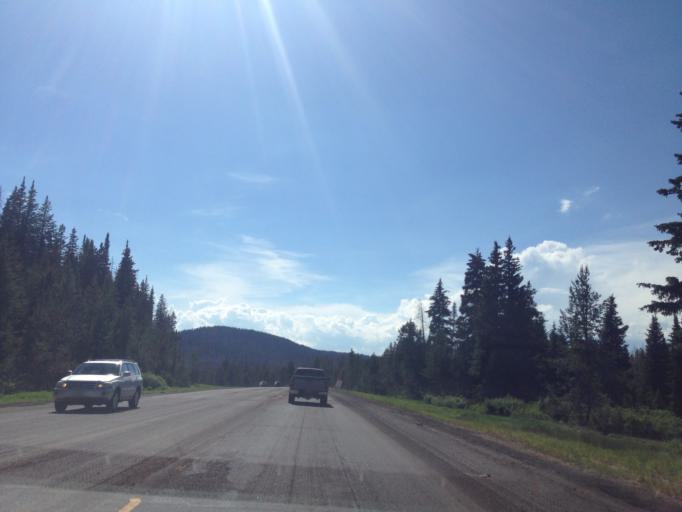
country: US
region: Colorado
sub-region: Routt County
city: Steamboat Springs
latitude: 40.3843
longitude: -106.7044
